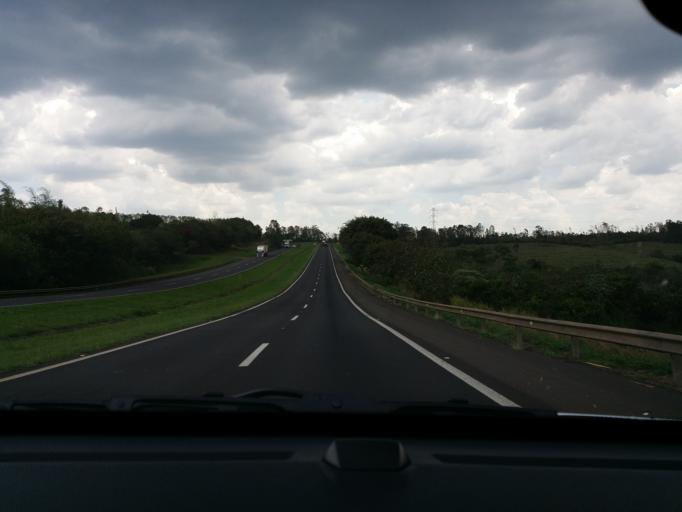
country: BR
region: Sao Paulo
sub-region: Rio Claro
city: Rio Claro
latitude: -22.3176
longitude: -47.6595
